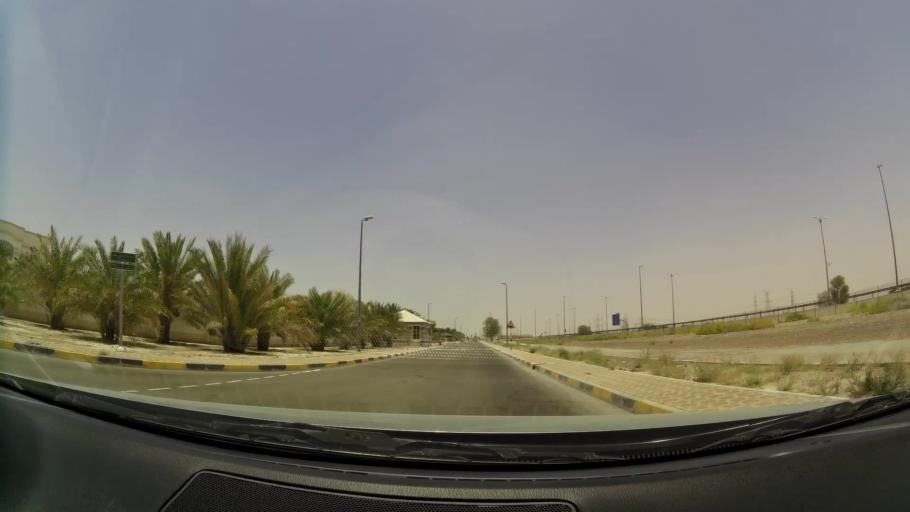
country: OM
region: Al Buraimi
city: Al Buraymi
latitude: 24.2787
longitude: 55.7296
